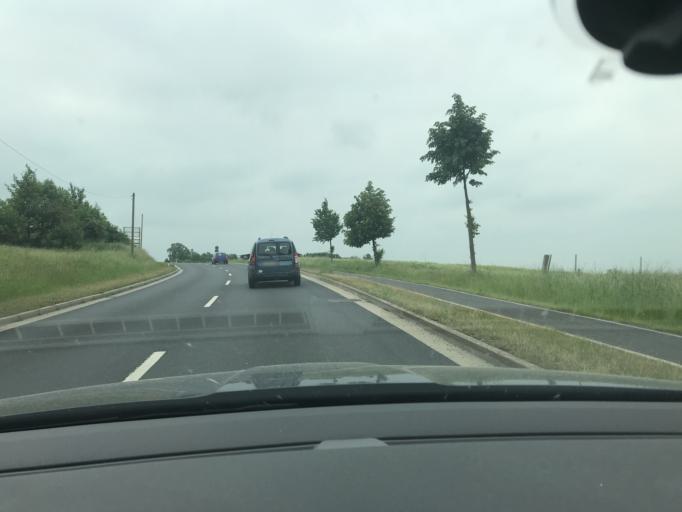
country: DE
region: Saxony
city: Priestewitz
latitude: 51.2271
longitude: 13.5051
